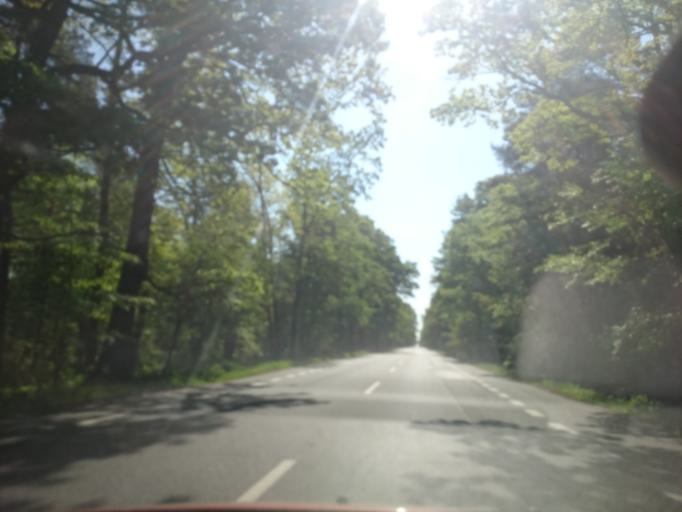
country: PL
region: Opole Voivodeship
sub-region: Powiat opolski
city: Chrzastowice
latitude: 50.6342
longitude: 18.0152
